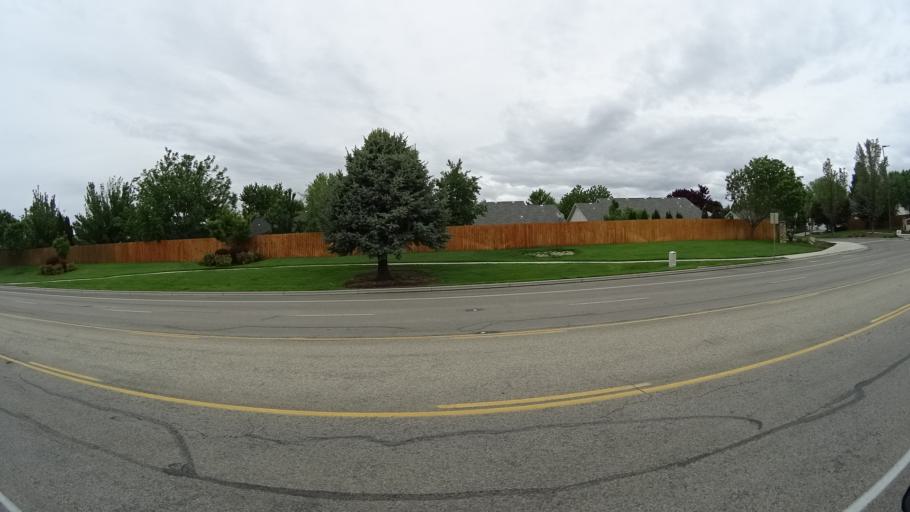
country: US
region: Idaho
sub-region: Ada County
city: Meridian
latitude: 43.6338
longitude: -116.3475
